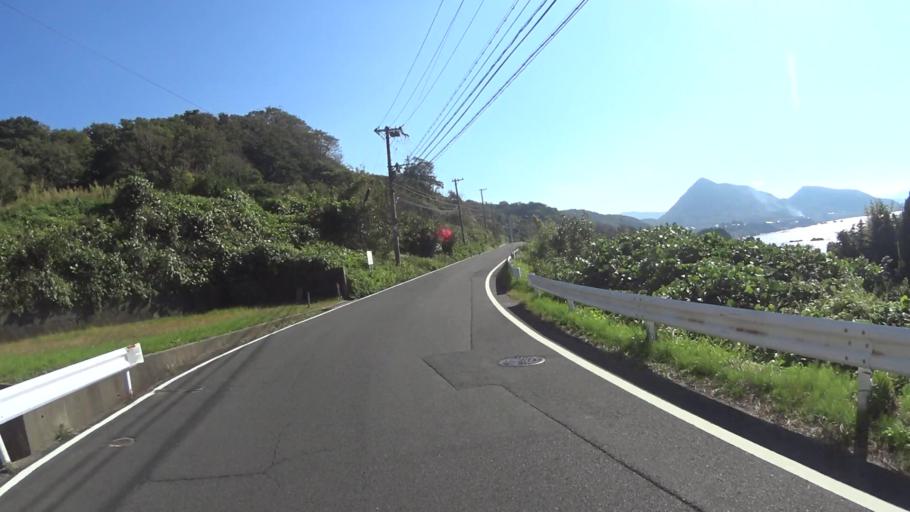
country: JP
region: Kyoto
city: Miyazu
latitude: 35.7328
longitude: 135.0883
